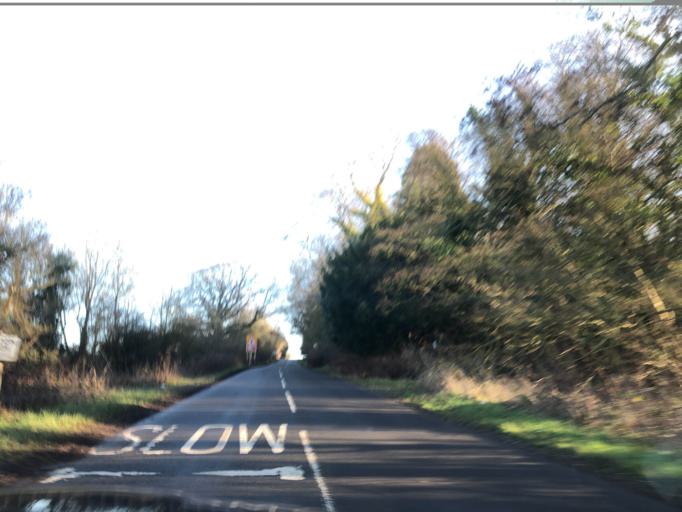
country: GB
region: England
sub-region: Warwickshire
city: Wellesbourne Mountford
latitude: 52.1901
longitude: -1.5581
